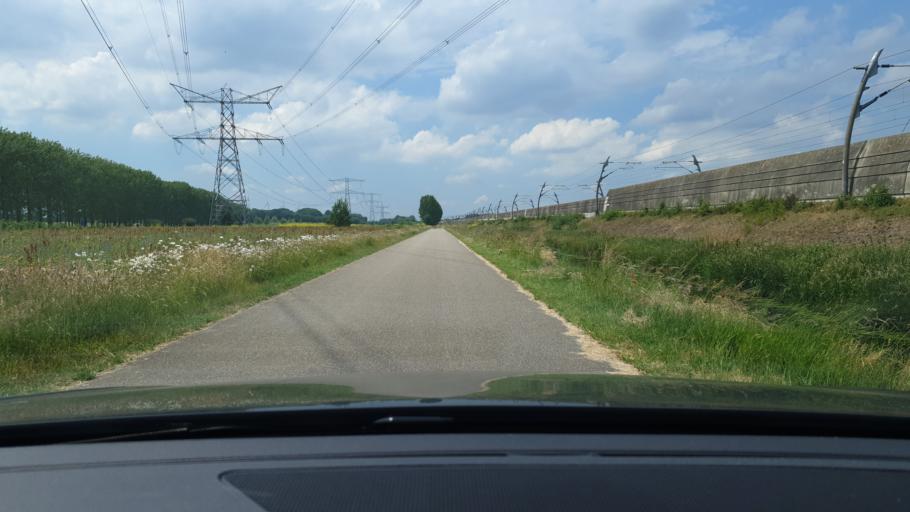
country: NL
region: Gelderland
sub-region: Gemeente Overbetuwe
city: Elst
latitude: 51.9007
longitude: 5.8874
